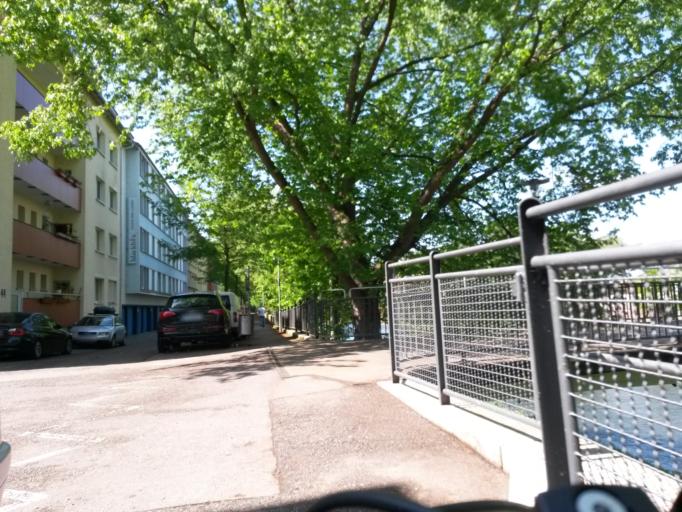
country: DE
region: Baden-Wuerttemberg
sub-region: Karlsruhe Region
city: Pforzheim
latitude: 48.8887
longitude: 8.7072
